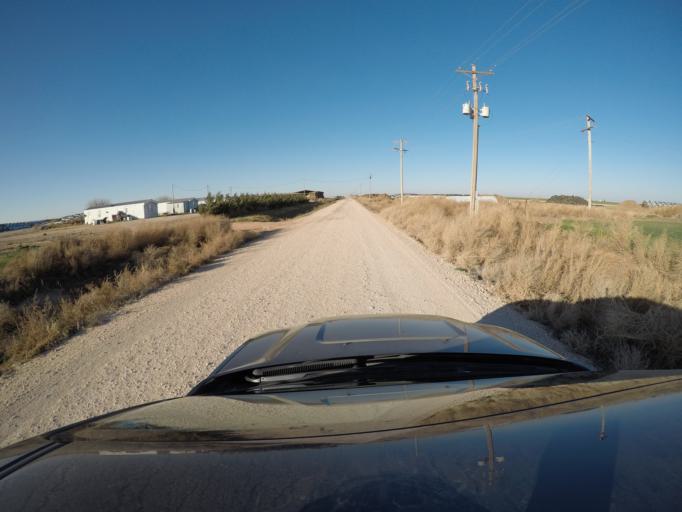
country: US
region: New Mexico
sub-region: Curry County
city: Texico
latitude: 34.3681
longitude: -103.1082
